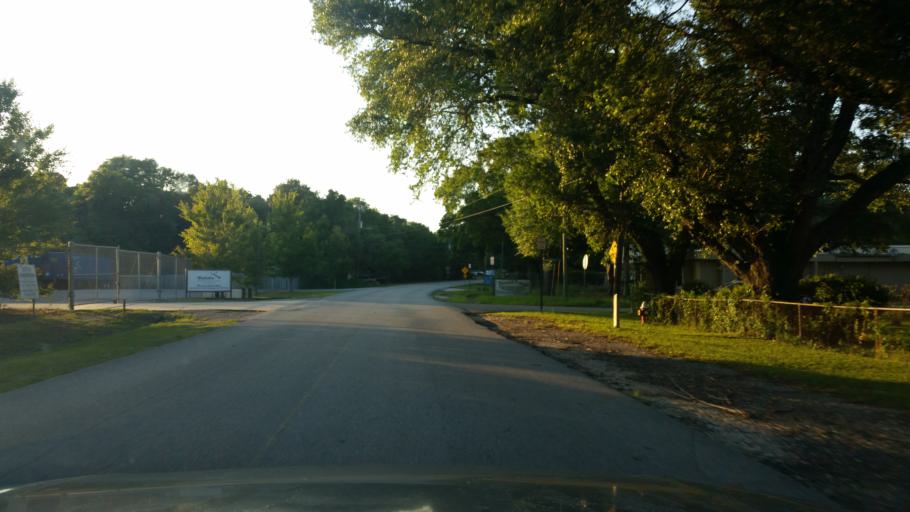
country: US
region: Florida
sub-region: Escambia County
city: Brent
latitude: 30.4620
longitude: -87.2282
